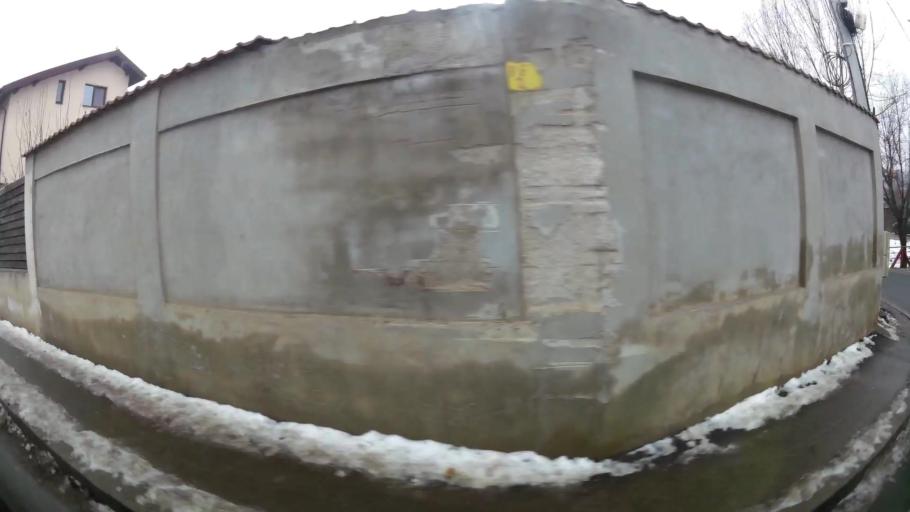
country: RO
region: Ilfov
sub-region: Comuna Chiajna
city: Rosu
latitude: 44.4429
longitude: 26.0068
